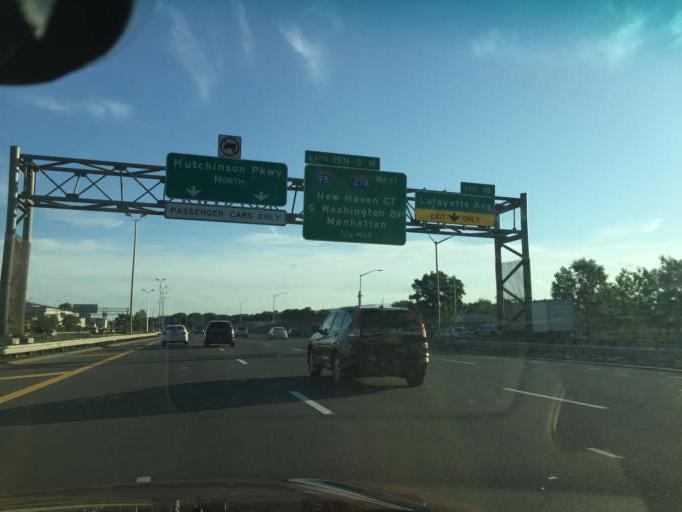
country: US
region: New York
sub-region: Bronx
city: The Bronx
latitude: 40.8169
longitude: -73.8362
